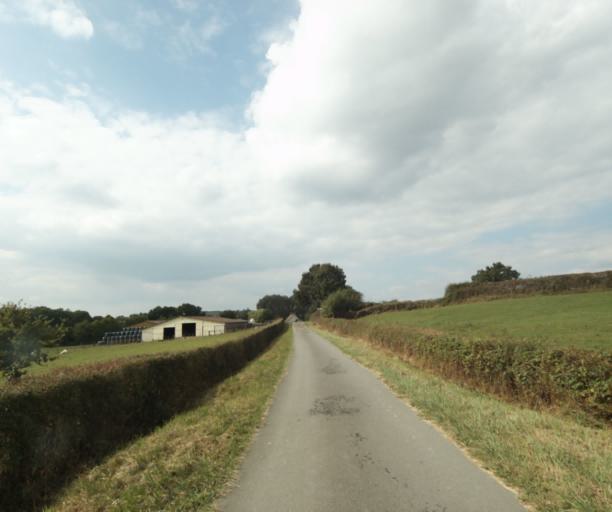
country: FR
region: Bourgogne
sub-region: Departement de Saone-et-Loire
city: Palinges
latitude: 46.5040
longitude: 4.1887
